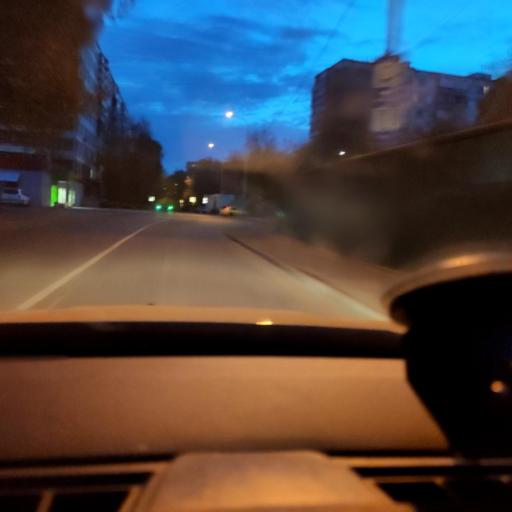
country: RU
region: Moscow
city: Yaroslavskiy
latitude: 55.8741
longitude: 37.7082
